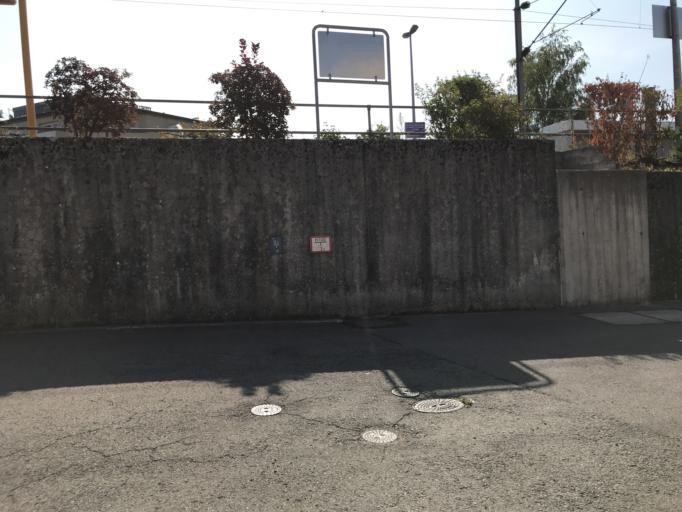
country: LU
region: Luxembourg
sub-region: Canton d'Esch-sur-Alzette
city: Niedercorn
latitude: 49.5369
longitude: 5.8940
